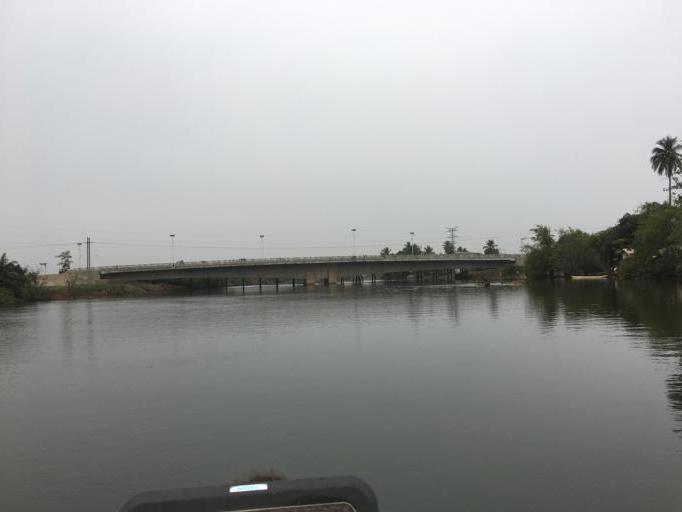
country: LR
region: Montserrado
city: Monrovia
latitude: 6.3744
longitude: -10.7798
